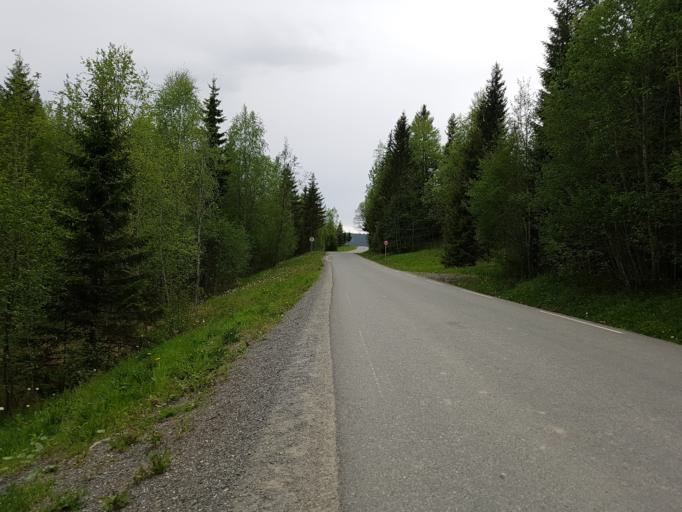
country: NO
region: Nord-Trondelag
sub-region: Levanger
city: Skogn
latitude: 63.6295
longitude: 11.2770
